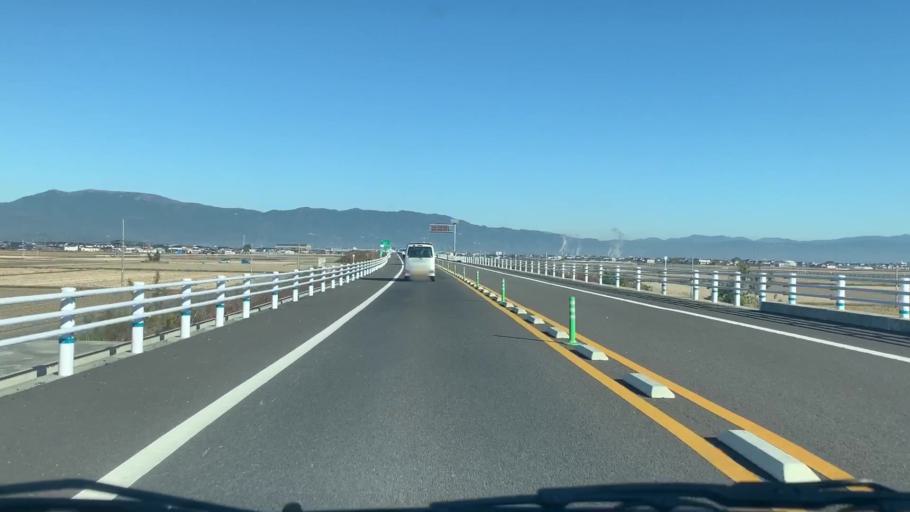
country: JP
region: Saga Prefecture
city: Saga-shi
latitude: 33.2069
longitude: 130.2151
